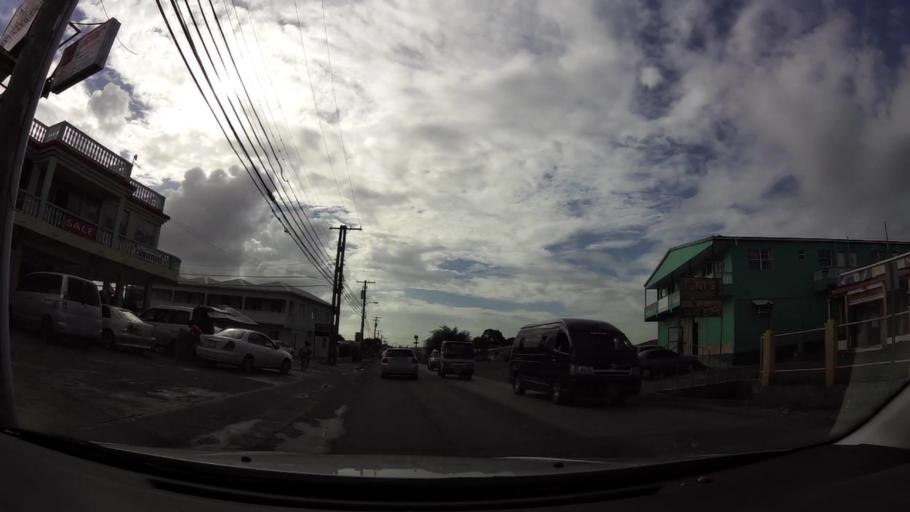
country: AG
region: Saint John
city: Saint John's
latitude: 17.1250
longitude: -61.8233
